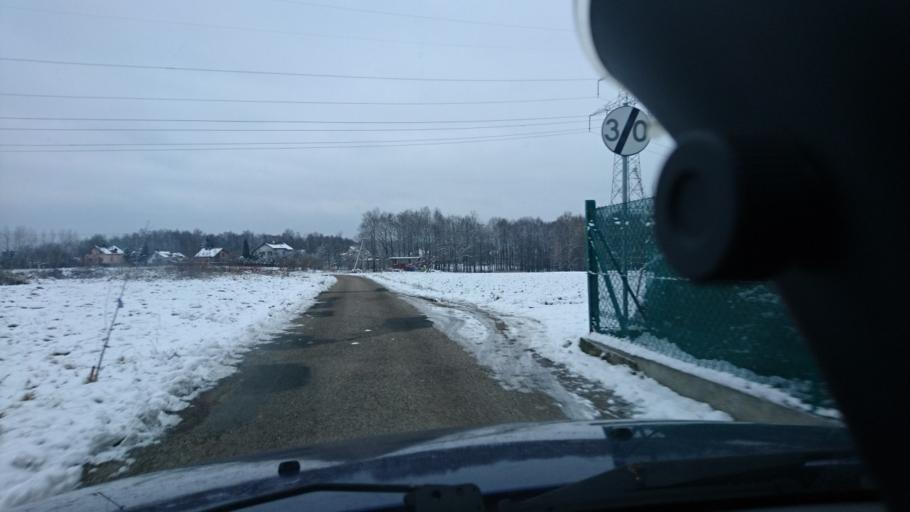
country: PL
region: Silesian Voivodeship
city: Janowice
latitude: 49.8623
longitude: 19.1106
